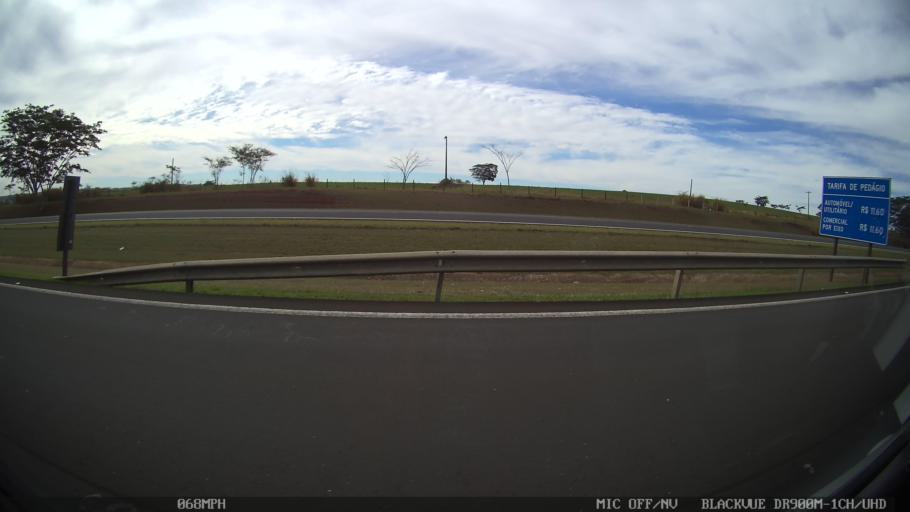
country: BR
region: Sao Paulo
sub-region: Santa Adelia
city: Santa Adelia
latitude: -21.3794
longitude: -48.7375
